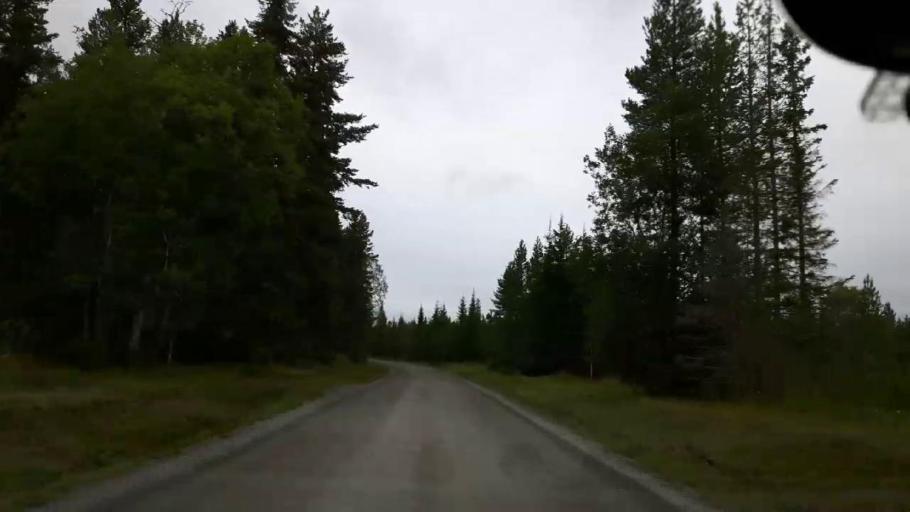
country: SE
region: Jaemtland
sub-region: OEstersunds Kommun
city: Ostersund
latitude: 63.1242
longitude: 14.5371
